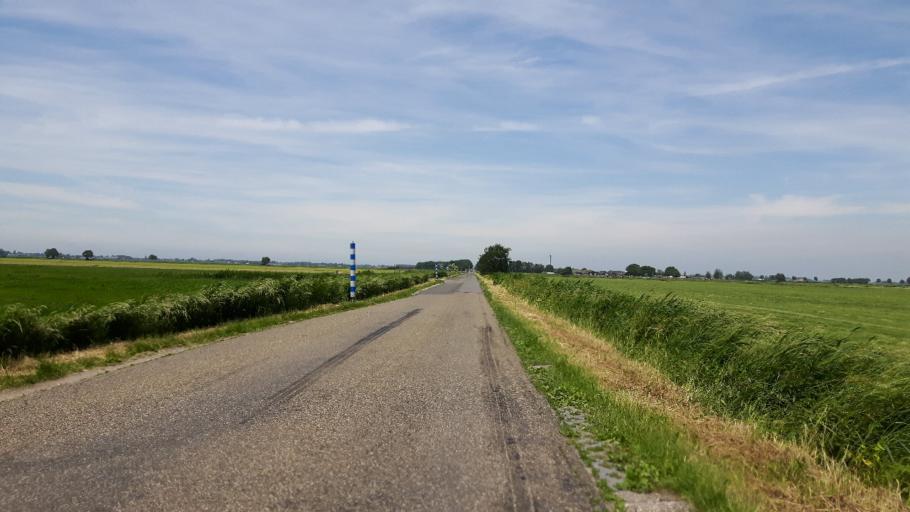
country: NL
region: South Holland
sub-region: Gemeente Nieuwkoop
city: Nieuwkoop
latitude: 52.1368
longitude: 4.7582
